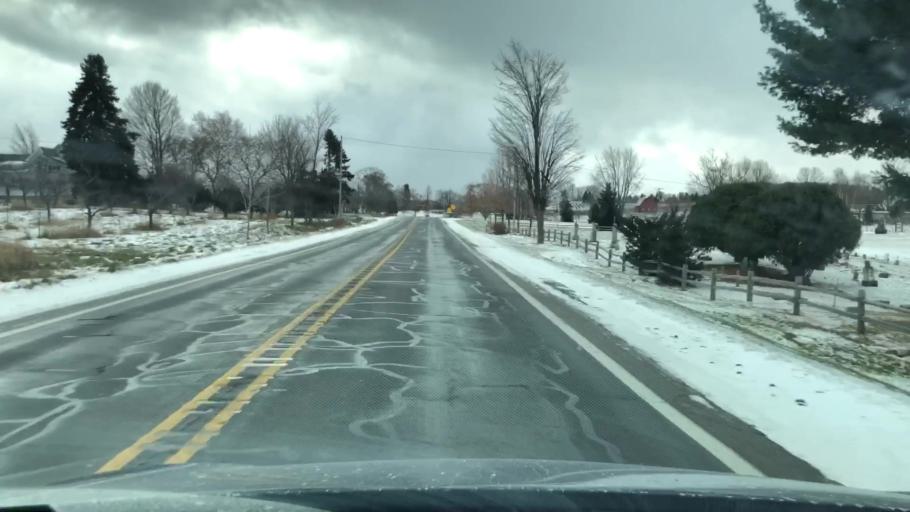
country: US
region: Michigan
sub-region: Antrim County
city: Elk Rapids
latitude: 44.8729
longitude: -85.5153
